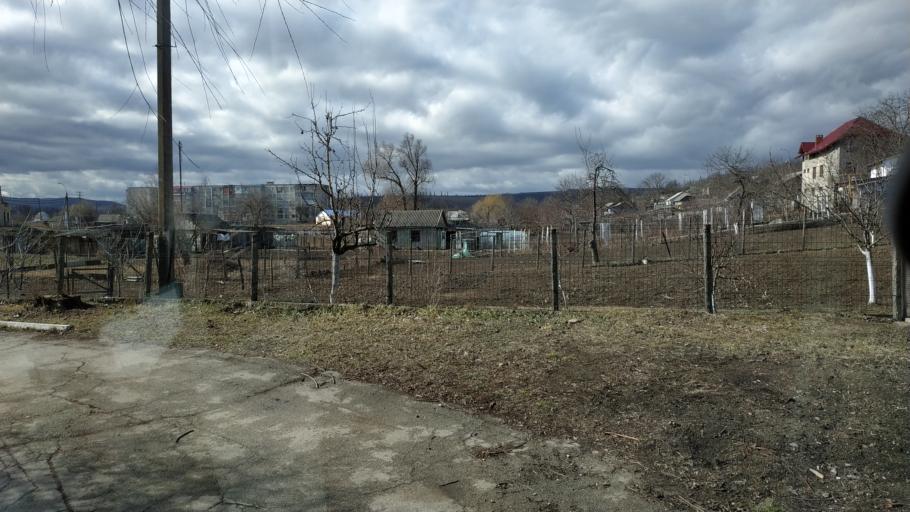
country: MD
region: Stinga Nistrului
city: Bucovat
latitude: 47.1875
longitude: 28.4733
